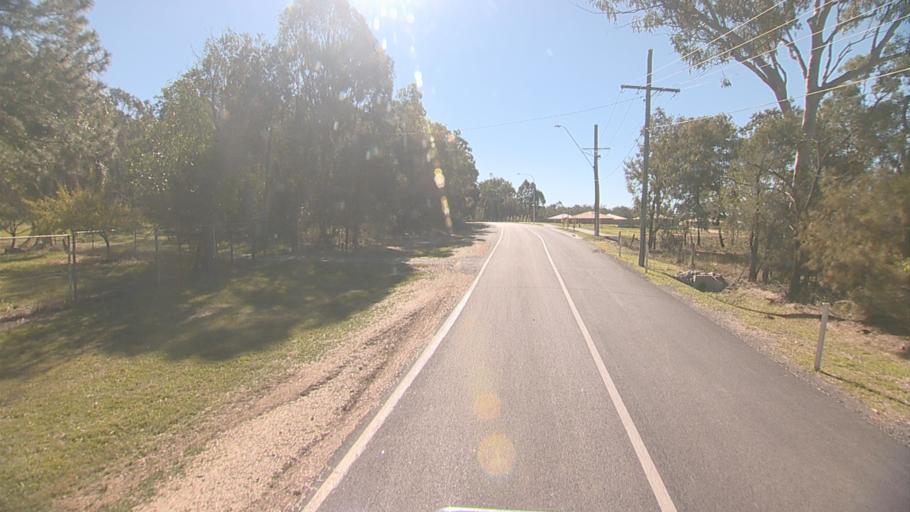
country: AU
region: Queensland
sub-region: Logan
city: Logan Reserve
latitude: -27.7147
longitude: 153.0766
